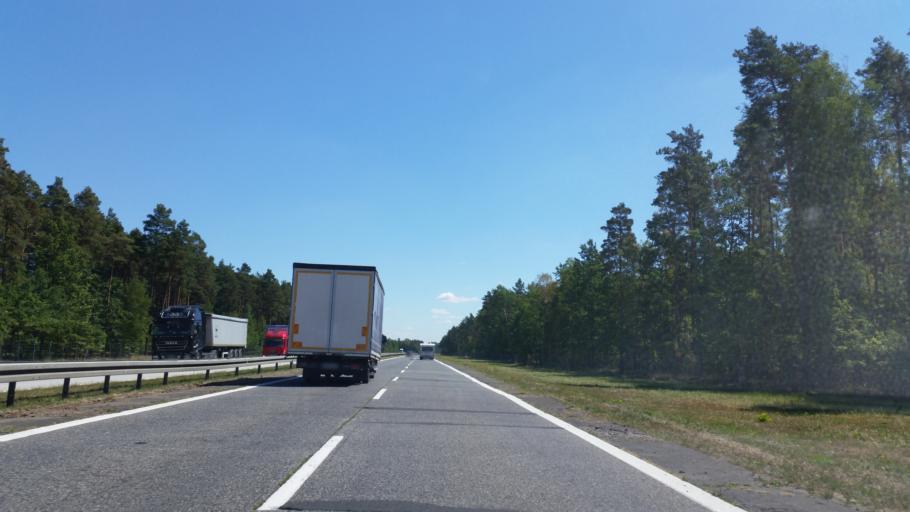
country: PL
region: Lubusz
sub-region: Powiat zarski
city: Lipinki Luzyckie
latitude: 51.6131
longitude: 14.9423
